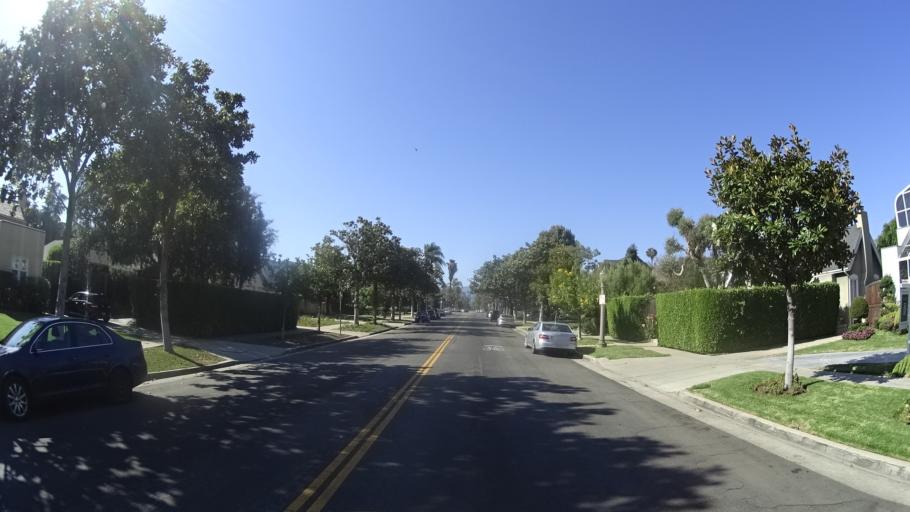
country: US
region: California
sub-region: Los Angeles County
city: Hollywood
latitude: 34.0750
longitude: -118.3259
